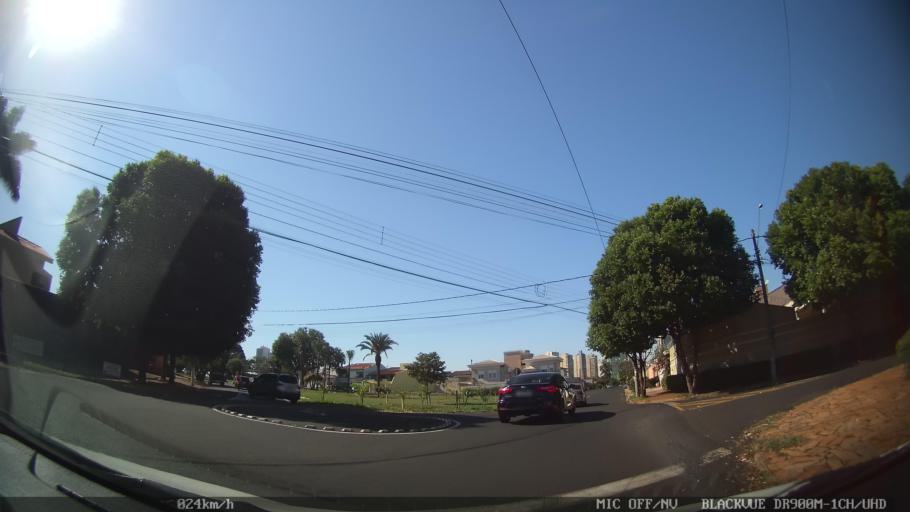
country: BR
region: Sao Paulo
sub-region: Ribeirao Preto
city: Ribeirao Preto
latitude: -21.2013
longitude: -47.8162
